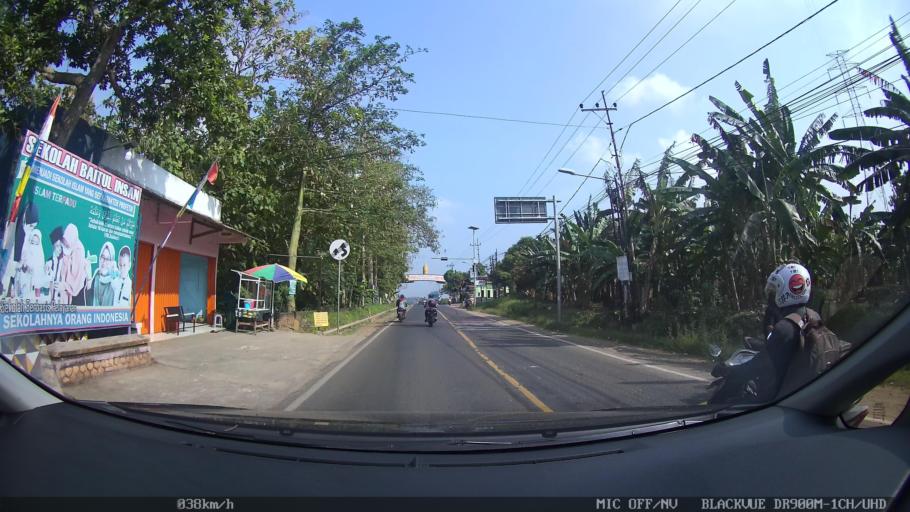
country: ID
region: Lampung
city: Kedaton
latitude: -5.3866
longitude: 105.2023
